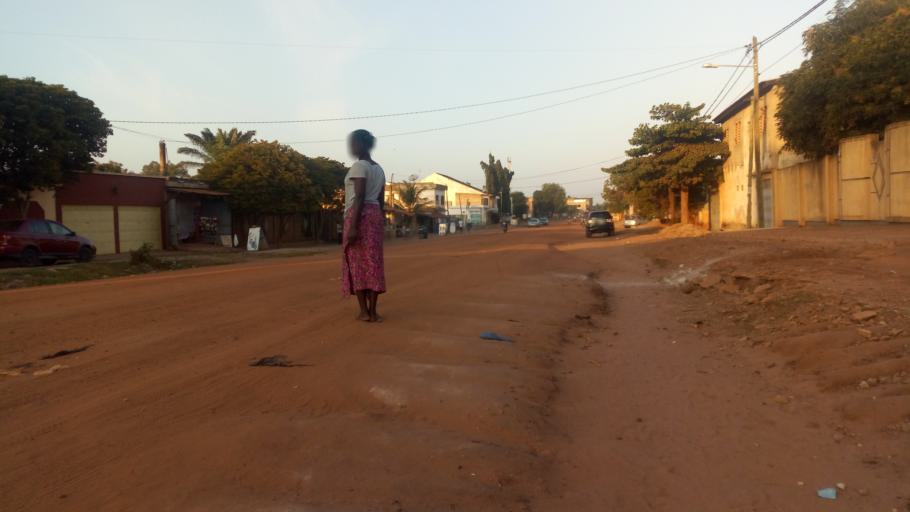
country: TG
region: Maritime
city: Lome
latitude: 6.1921
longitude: 1.1915
